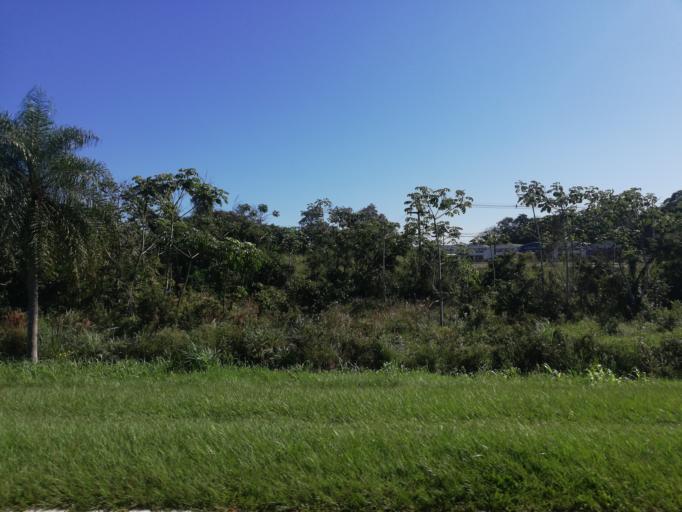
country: AR
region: Misiones
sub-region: Departamento de Iguazu
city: Puerto Iguazu
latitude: -25.5774
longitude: -54.5555
